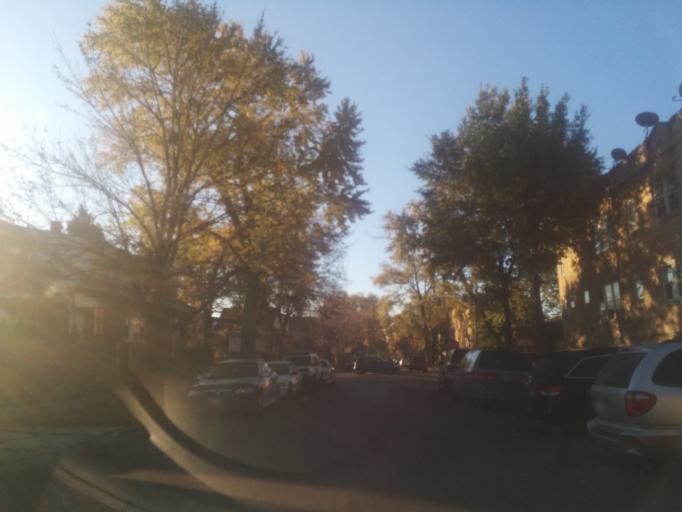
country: US
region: Illinois
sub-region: Cook County
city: Elmwood Park
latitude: 41.9347
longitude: -87.7516
